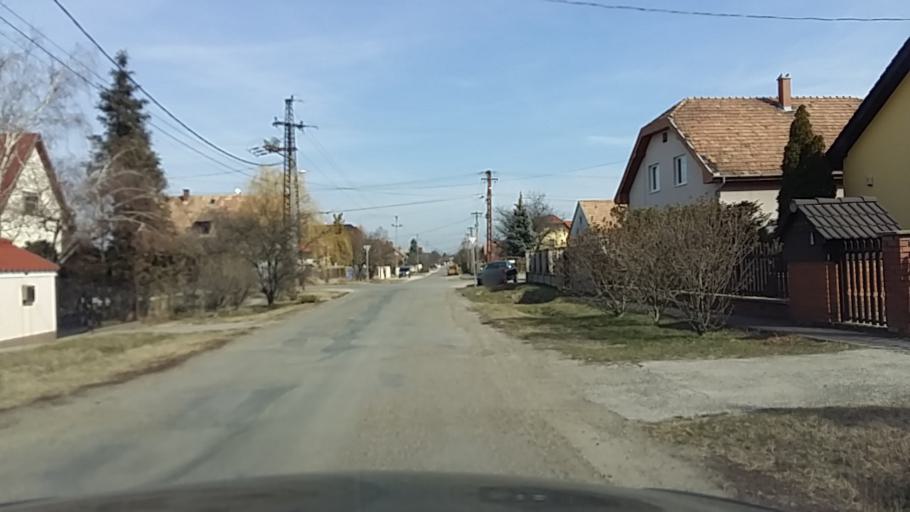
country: HU
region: Pest
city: Szigetszentmiklos
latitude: 47.3489
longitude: 19.0183
